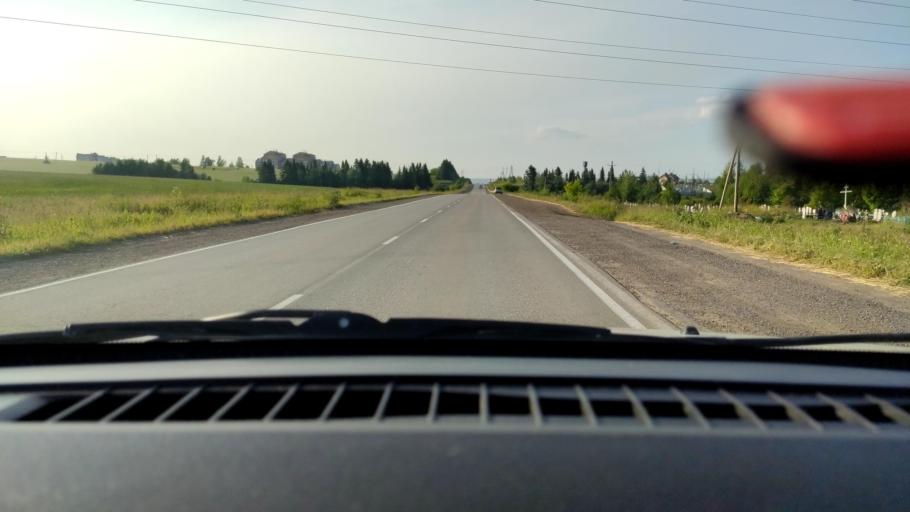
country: RU
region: Perm
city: Lobanovo
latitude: 57.8537
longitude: 56.2962
